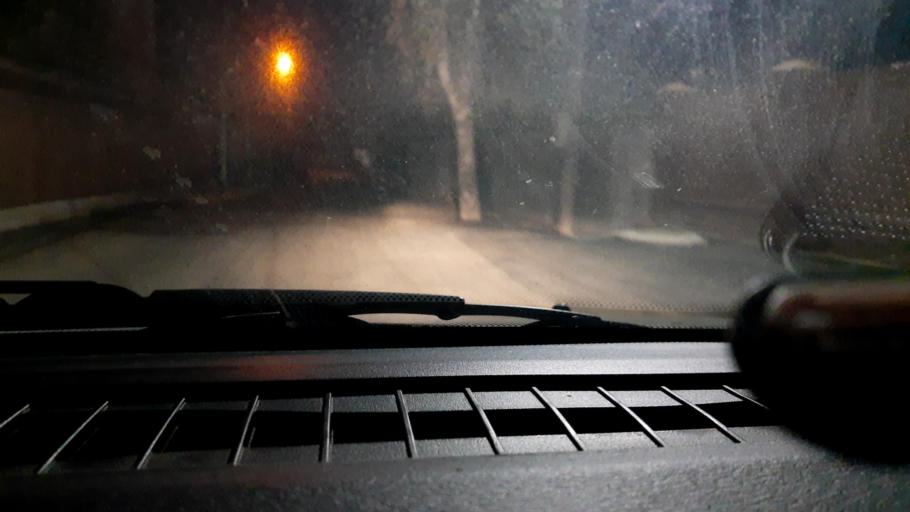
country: RU
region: Nizjnij Novgorod
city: Nizhniy Novgorod
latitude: 56.2984
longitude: 43.9204
